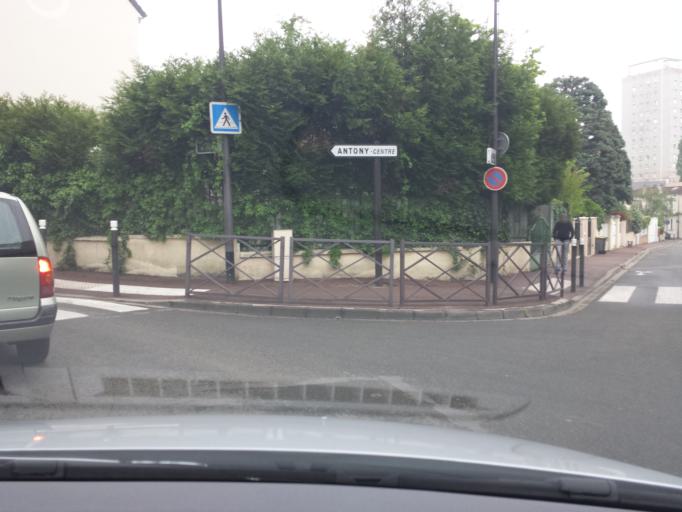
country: FR
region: Ile-de-France
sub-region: Departement des Hauts-de-Seine
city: Antony
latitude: 48.7510
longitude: 2.2965
